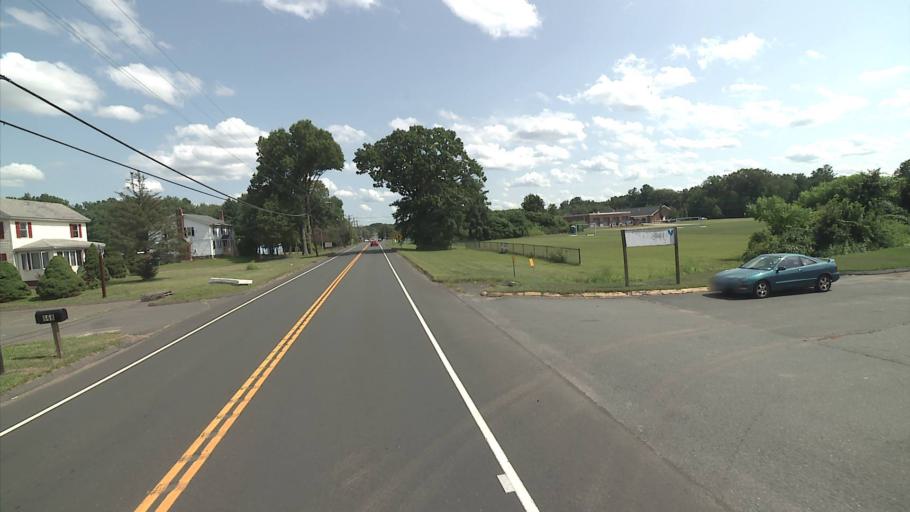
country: US
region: Connecticut
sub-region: Hartford County
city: South Windsor
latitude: 41.8501
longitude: -72.5758
